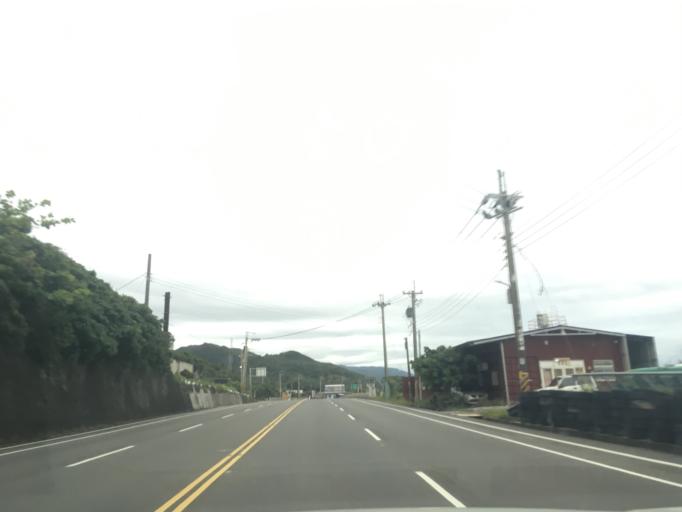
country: TW
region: Taiwan
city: Hengchun
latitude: 22.3011
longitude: 120.8888
